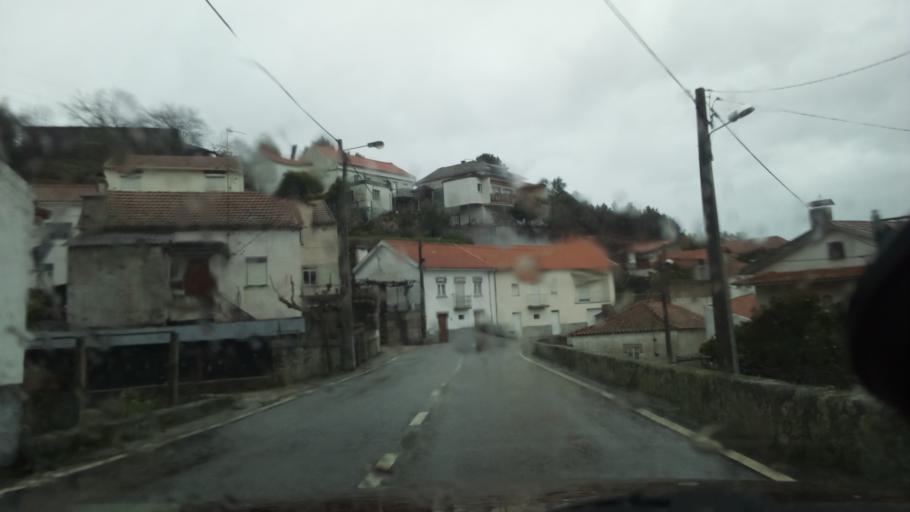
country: PT
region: Guarda
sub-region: Fornos de Algodres
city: Fornos de Algodres
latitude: 40.5172
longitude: -7.5815
